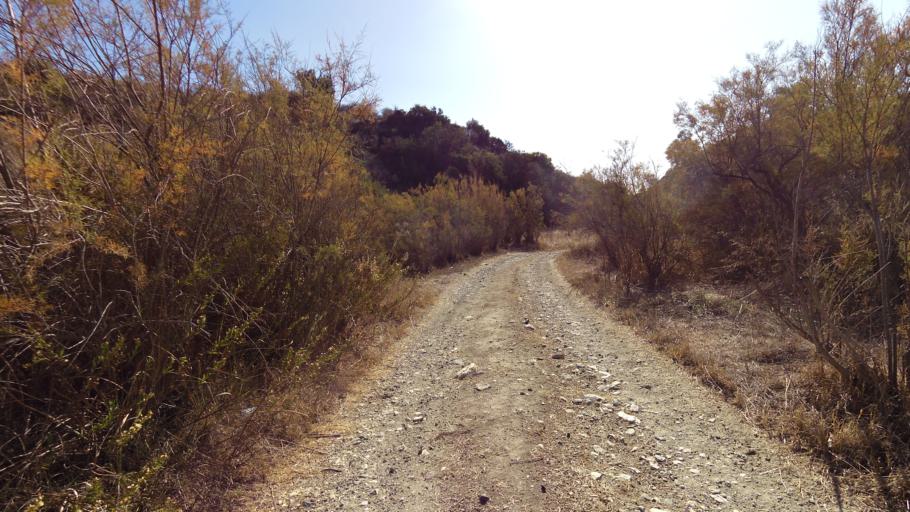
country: CY
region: Limassol
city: Mouttagiaka
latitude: 34.7584
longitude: 33.0847
